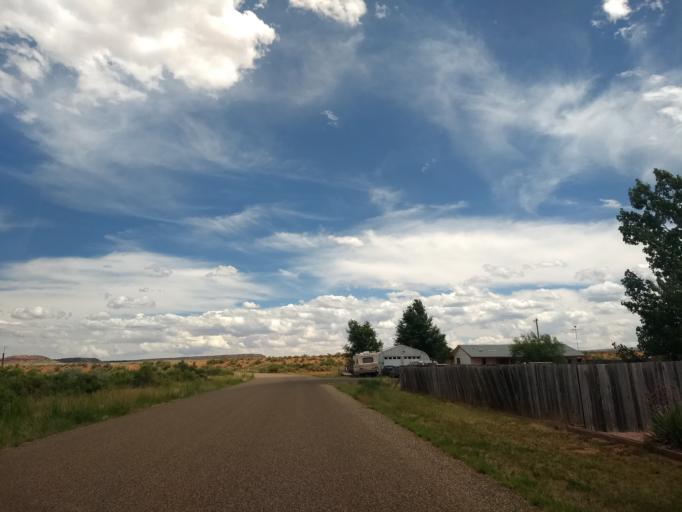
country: US
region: Arizona
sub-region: Coconino County
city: Fredonia
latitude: 36.9614
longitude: -112.5235
